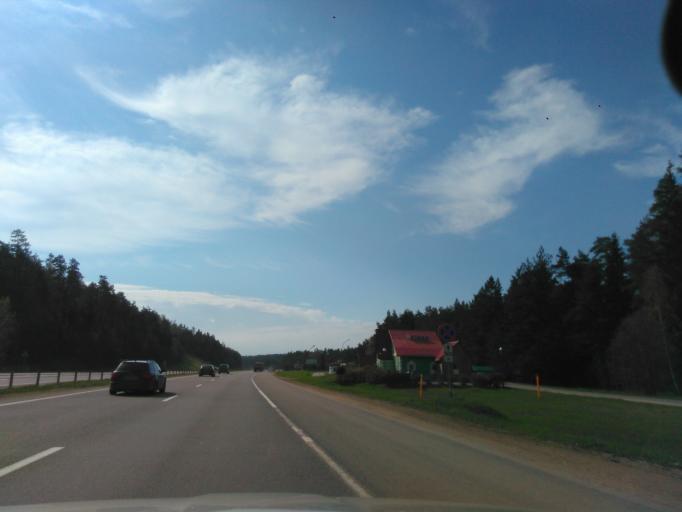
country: BY
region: Minsk
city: Rakaw
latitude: 53.9541
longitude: 27.1148
